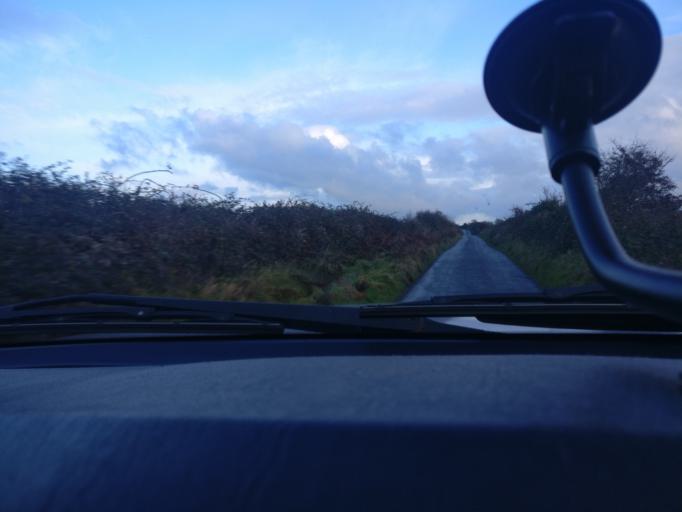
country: IE
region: Connaught
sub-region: County Galway
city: Athenry
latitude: 53.1978
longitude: -8.6935
